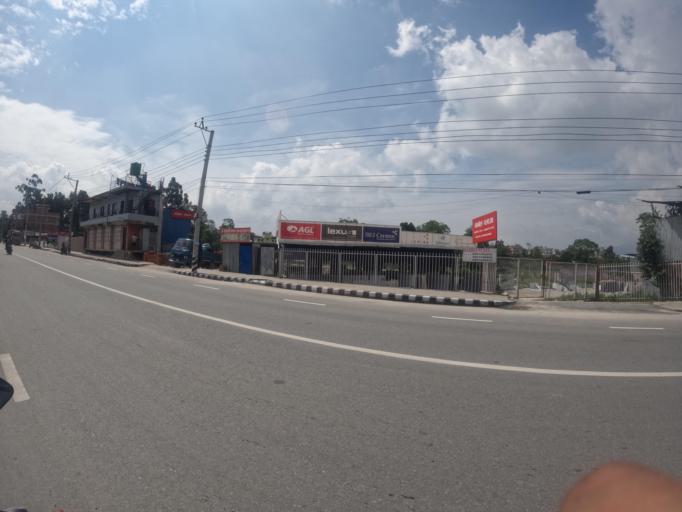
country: NP
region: Central Region
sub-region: Bagmati Zone
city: Kathmandu
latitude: 27.6848
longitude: 85.3668
